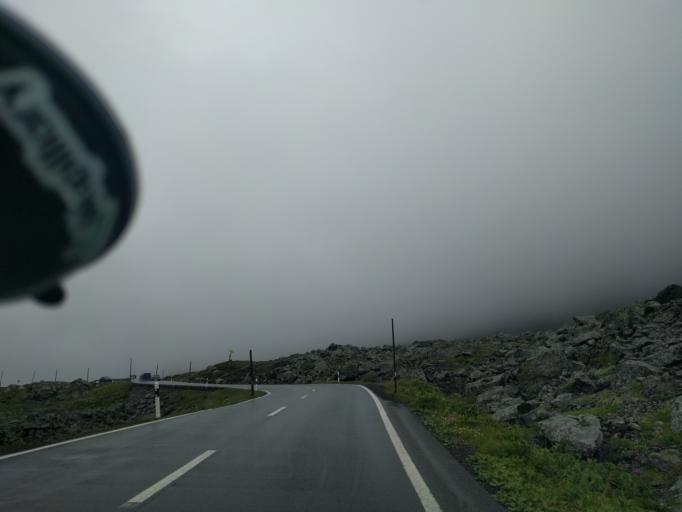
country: CH
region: Grisons
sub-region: Praettigau/Davos District
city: Davos
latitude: 46.7534
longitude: 9.9428
